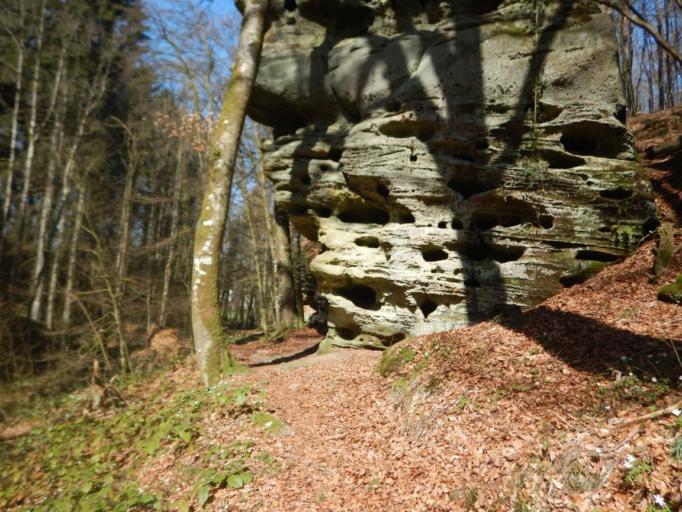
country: LU
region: Grevenmacher
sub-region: Canton d'Echternach
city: Consdorf
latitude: 49.7790
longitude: 6.3575
